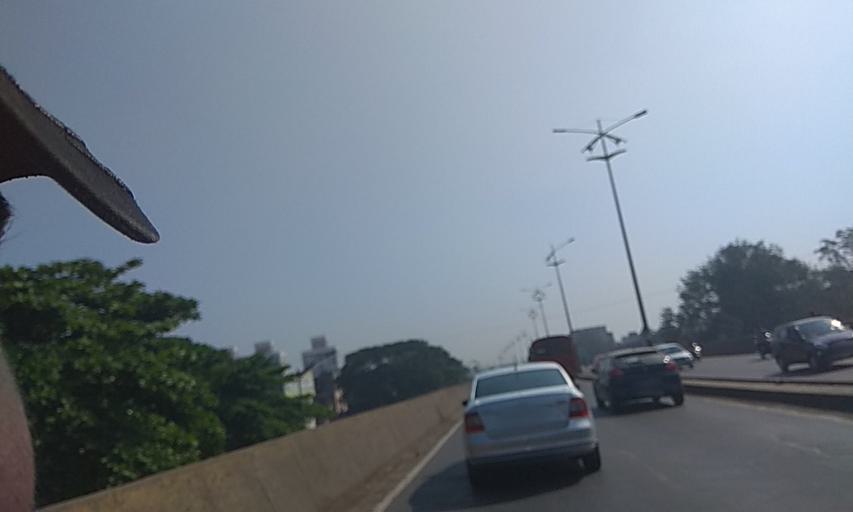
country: IN
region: Maharashtra
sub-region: Pune Division
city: Pune
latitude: 18.5013
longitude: 73.9347
